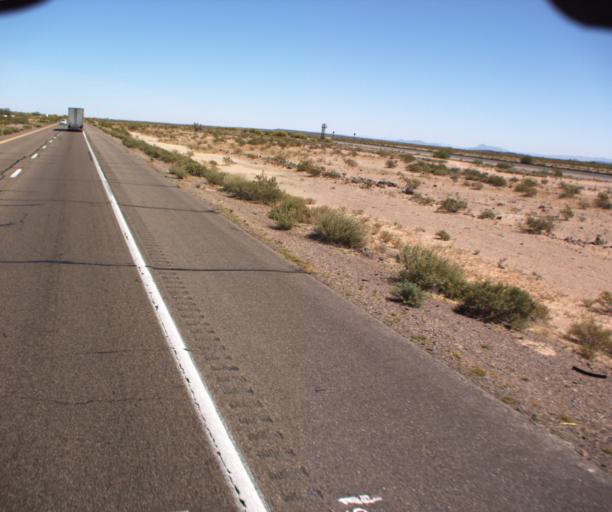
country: US
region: Arizona
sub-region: Maricopa County
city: Gila Bend
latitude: 32.8635
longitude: -113.1651
